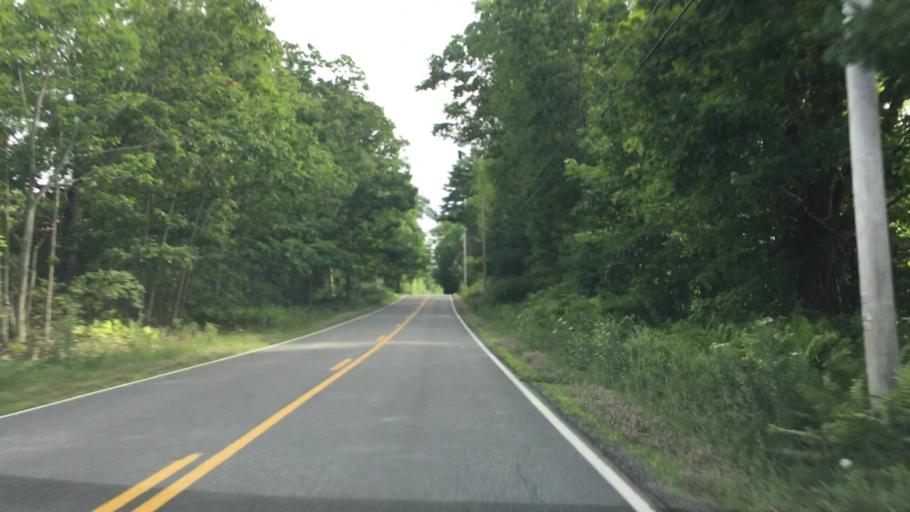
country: US
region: Maine
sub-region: Waldo County
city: Belfast
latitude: 44.3932
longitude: -69.0328
